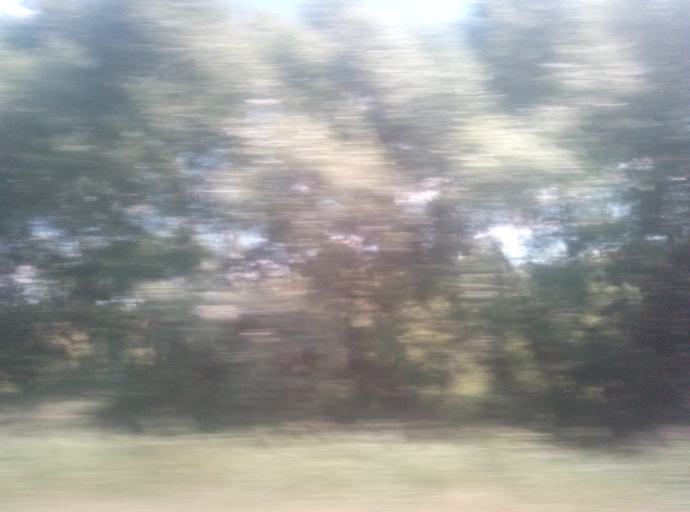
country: RU
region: Tula
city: Kireyevsk
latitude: 53.9725
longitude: 37.9302
